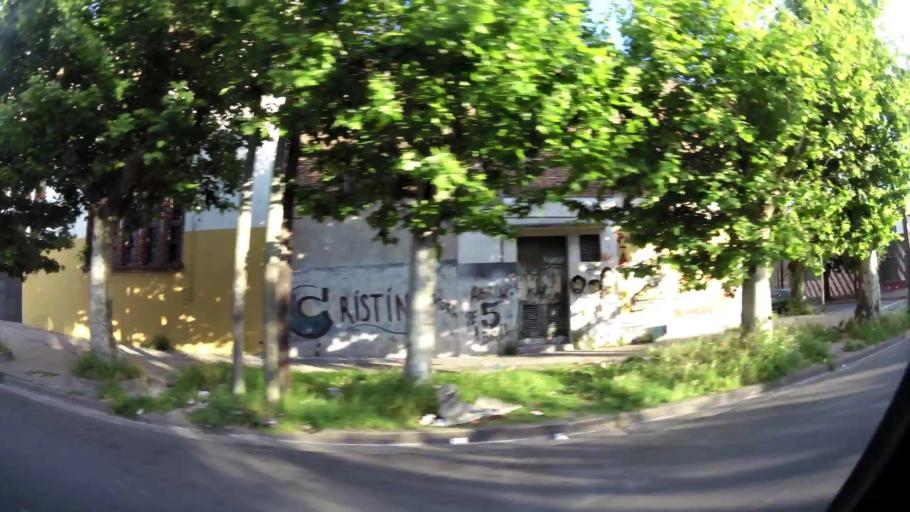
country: AR
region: Buenos Aires
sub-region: Partido de Avellaneda
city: Avellaneda
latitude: -34.6952
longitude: -58.3316
